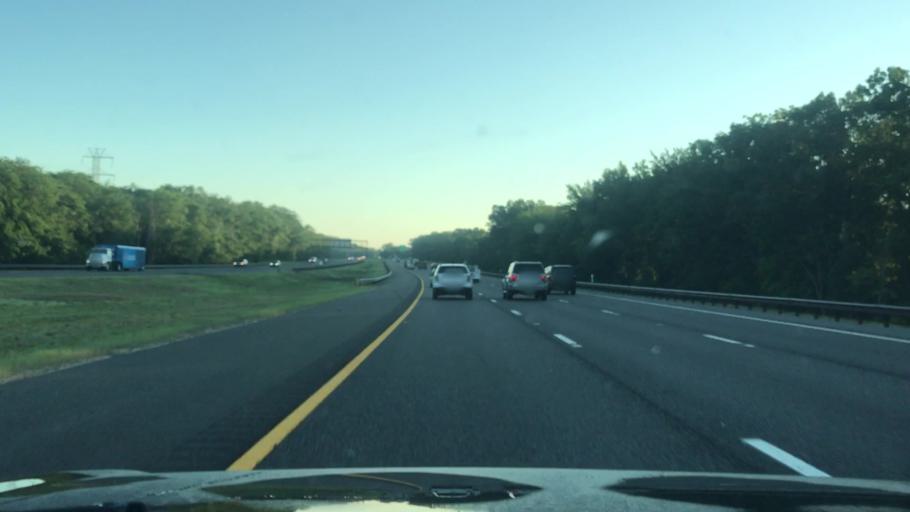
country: US
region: New Jersey
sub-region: Ocean County
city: Leisure Village East
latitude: 40.0195
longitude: -74.1845
